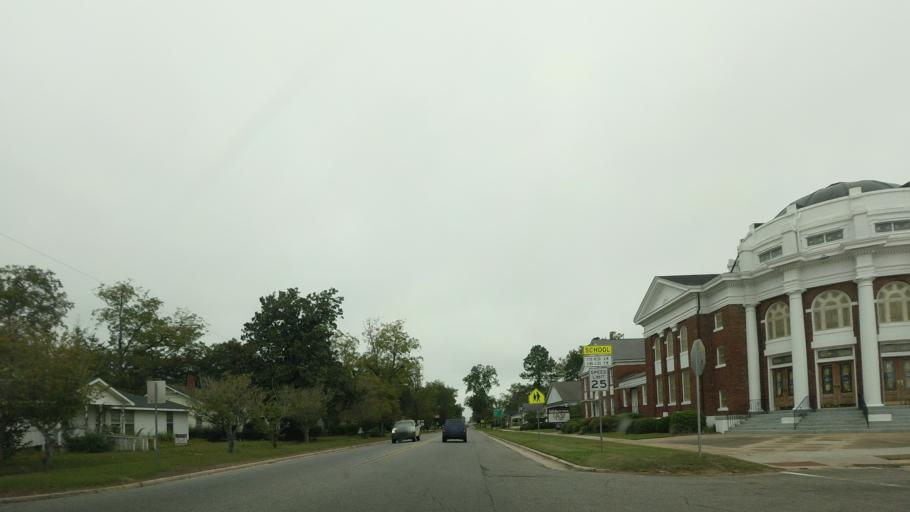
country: US
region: Georgia
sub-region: Irwin County
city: Ocilla
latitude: 31.5956
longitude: -83.2505
